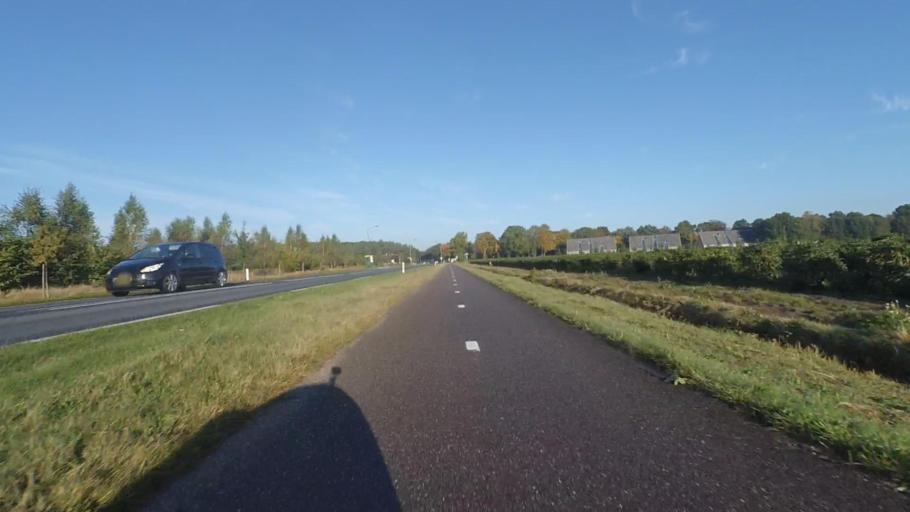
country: NL
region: Gelderland
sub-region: Gemeente Apeldoorn
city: Uddel
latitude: 52.2393
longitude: 5.7645
